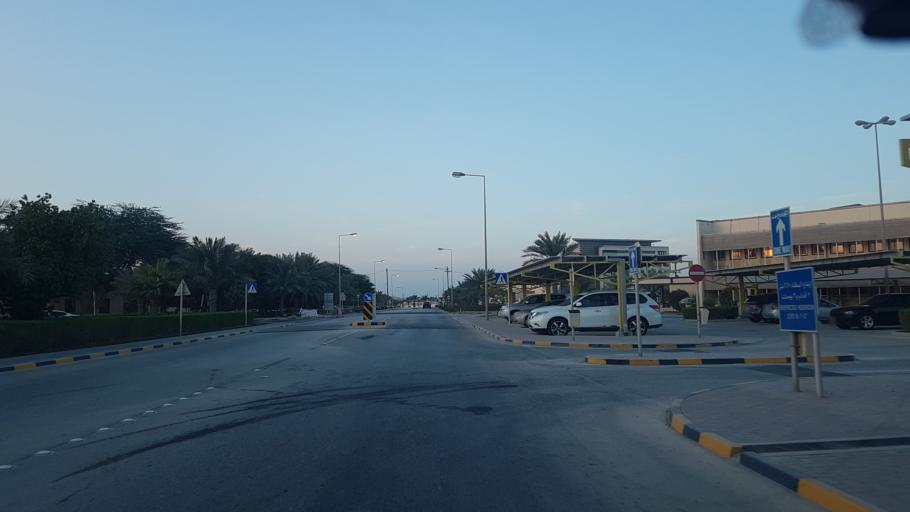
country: BH
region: Northern
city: Ar Rifa'
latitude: 26.0880
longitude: 50.5492
